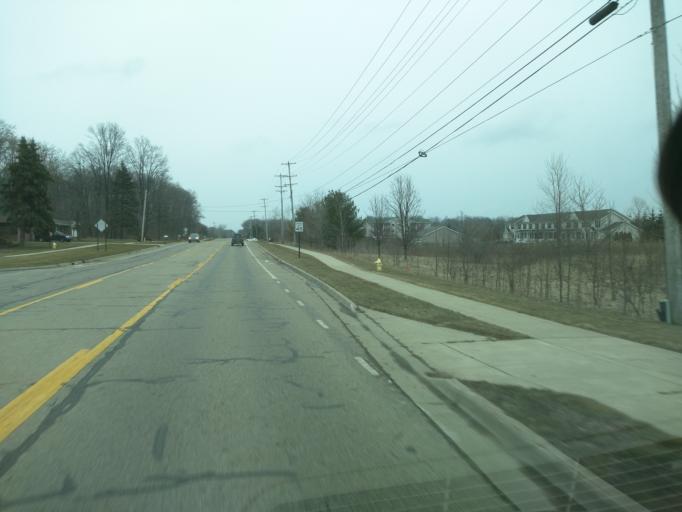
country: US
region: Michigan
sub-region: Eaton County
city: Waverly
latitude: 42.7555
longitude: -84.6610
